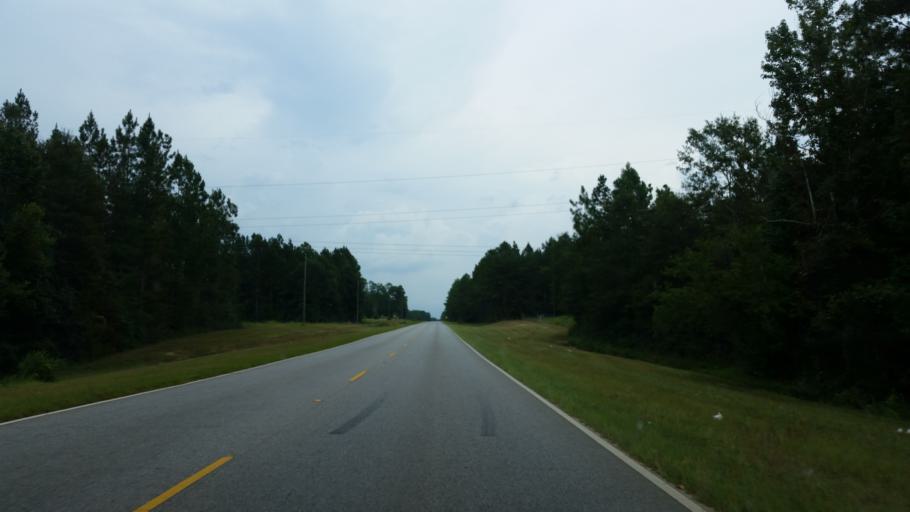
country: US
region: Florida
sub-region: Escambia County
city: Cantonment
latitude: 30.6545
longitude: -87.3135
